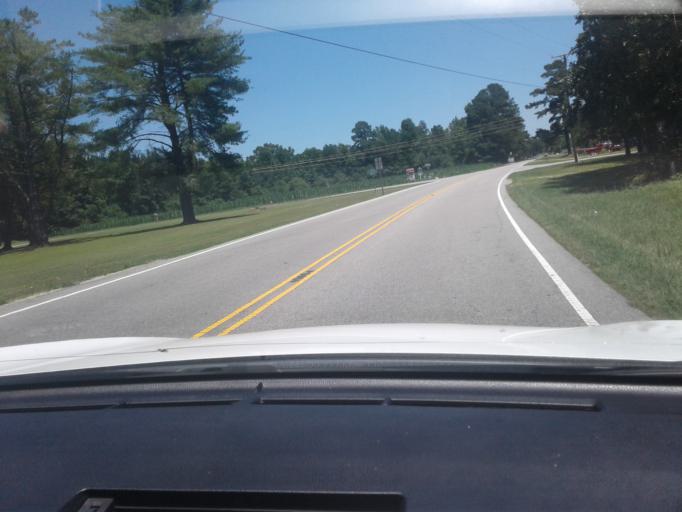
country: US
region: North Carolina
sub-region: Harnett County
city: Lillington
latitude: 35.3671
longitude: -78.8889
